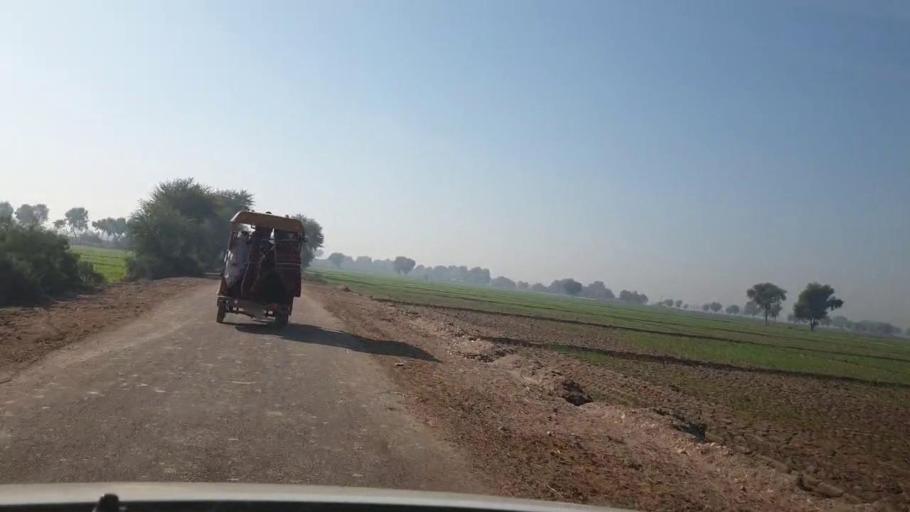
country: PK
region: Sindh
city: Dadu
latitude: 26.6453
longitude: 67.8215
